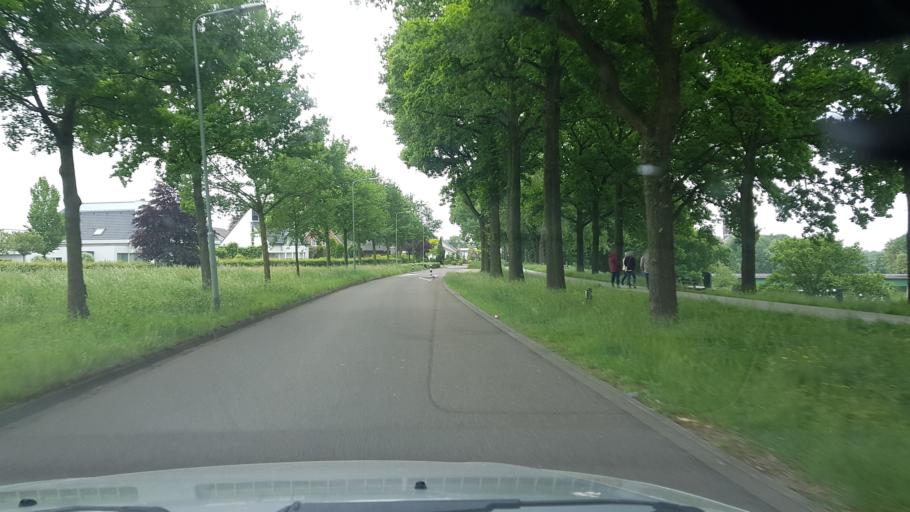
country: NL
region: Limburg
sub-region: Gemeente Stein
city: Elsloo
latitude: 50.9536
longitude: 5.7631
